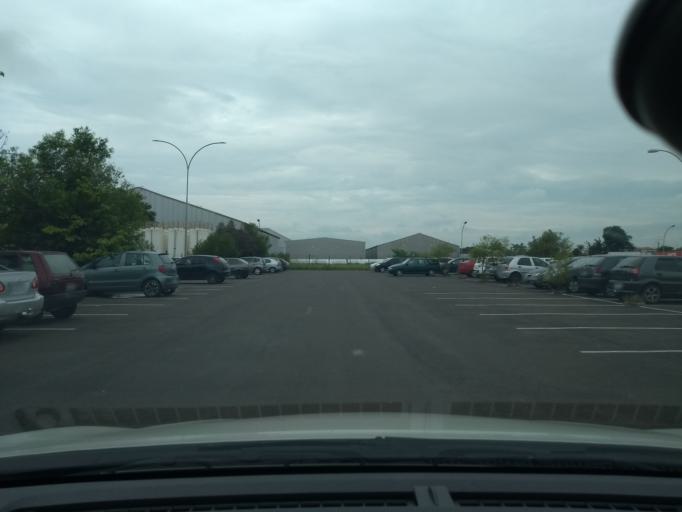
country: BR
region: Sao Paulo
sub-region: Rio Claro
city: Rio Claro
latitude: -22.3765
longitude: -47.5463
